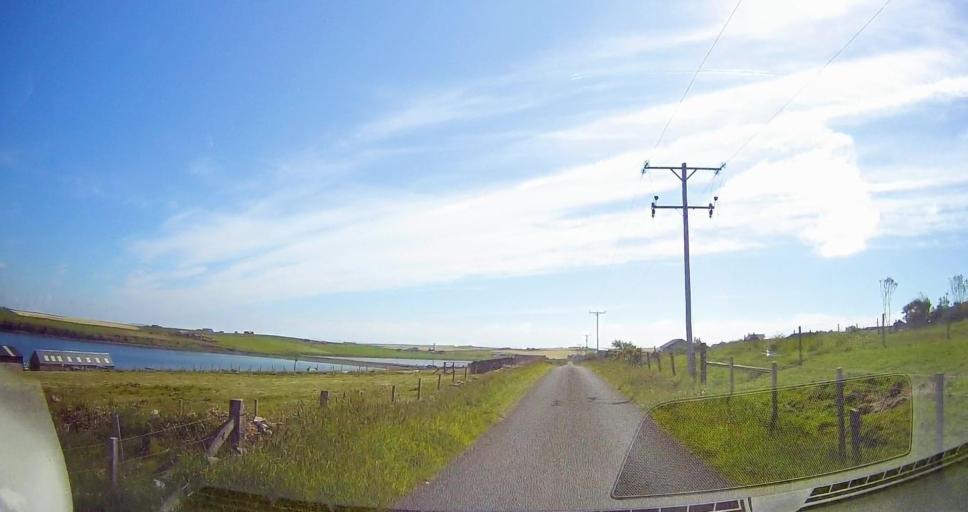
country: GB
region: Scotland
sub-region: Orkney Islands
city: Kirkwall
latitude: 58.8557
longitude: -2.9308
